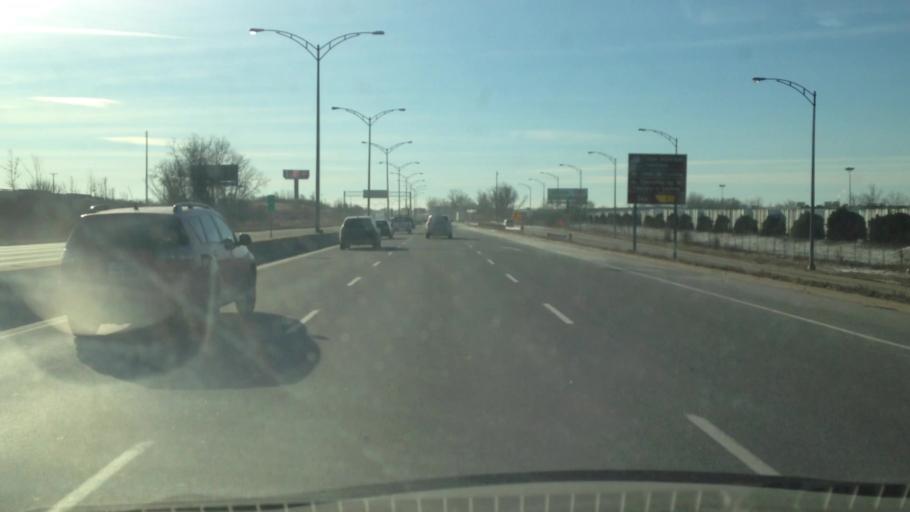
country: CA
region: Quebec
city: Cote-Saint-Luc
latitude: 45.4620
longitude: -73.6961
